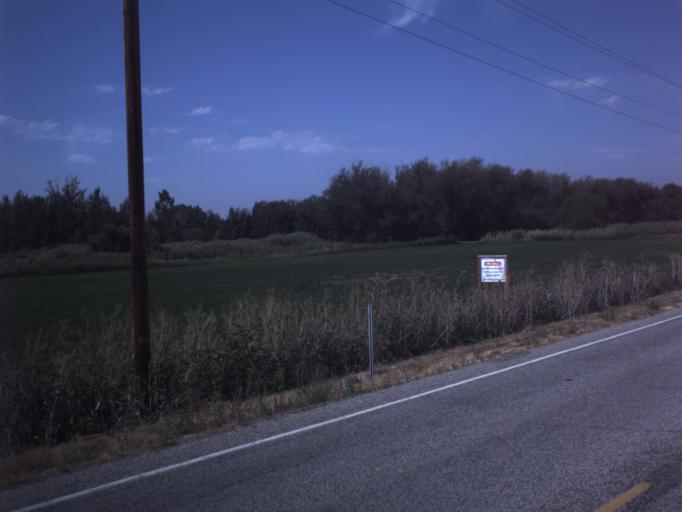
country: US
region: Utah
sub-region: Box Elder County
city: Willard
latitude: 41.4225
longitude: -112.0398
